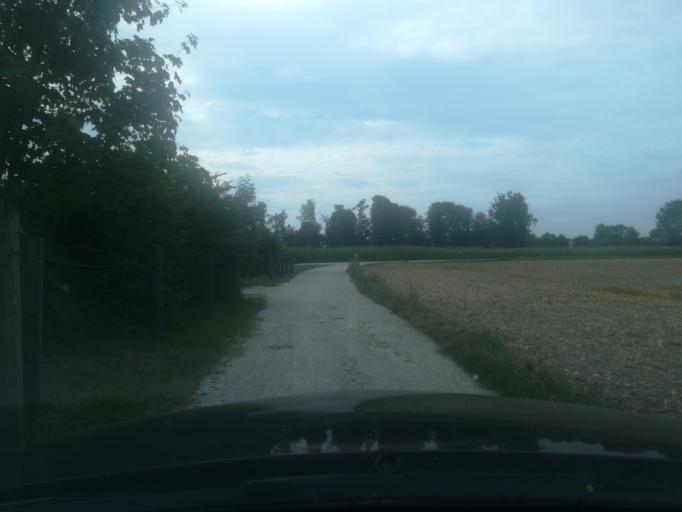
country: AT
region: Upper Austria
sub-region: Wels-Land
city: Marchtrenk
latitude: 48.1831
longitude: 14.1317
